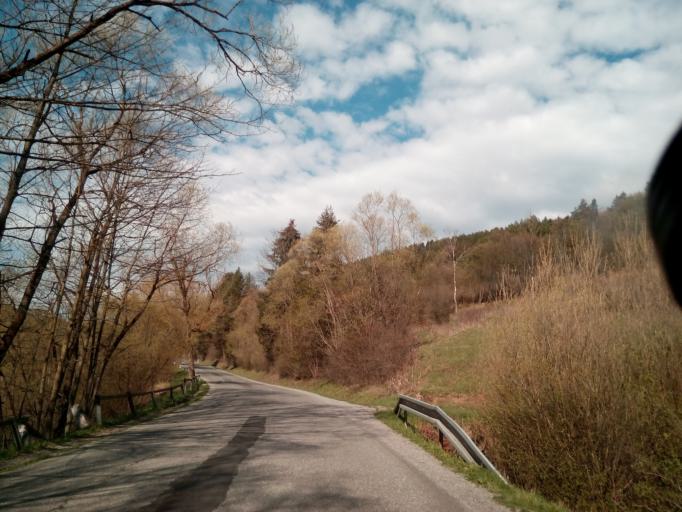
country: PL
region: Lesser Poland Voivodeship
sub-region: Powiat nowotarski
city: Niedzica
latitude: 49.3343
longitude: 20.3390
